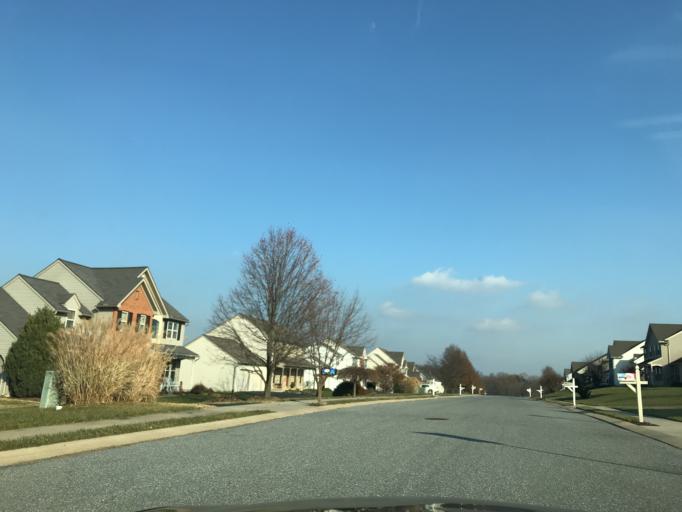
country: US
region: Pennsylvania
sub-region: York County
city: Loganville
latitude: 39.8585
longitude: -76.7133
